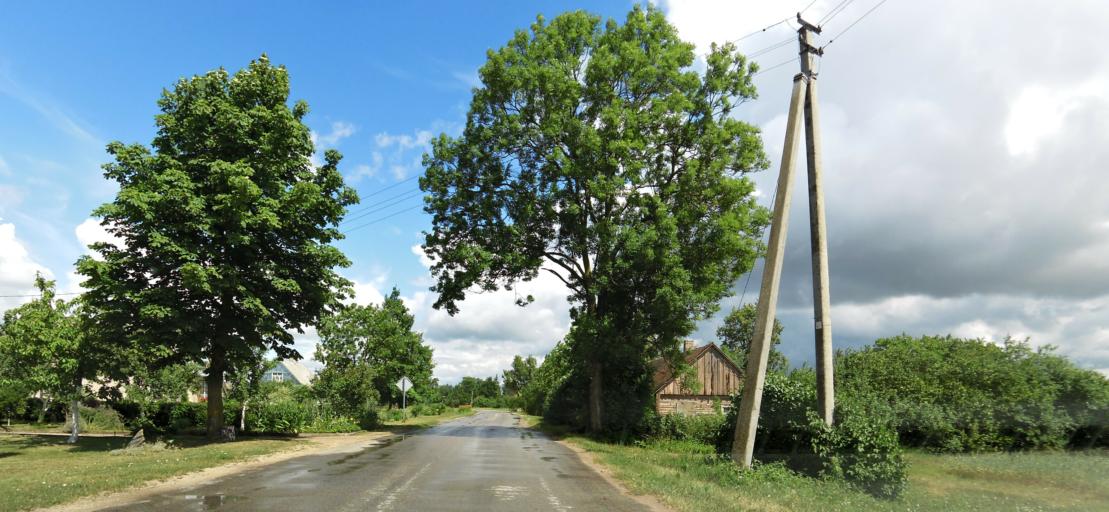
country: LT
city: Vabalninkas
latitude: 55.8810
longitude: 24.7807
